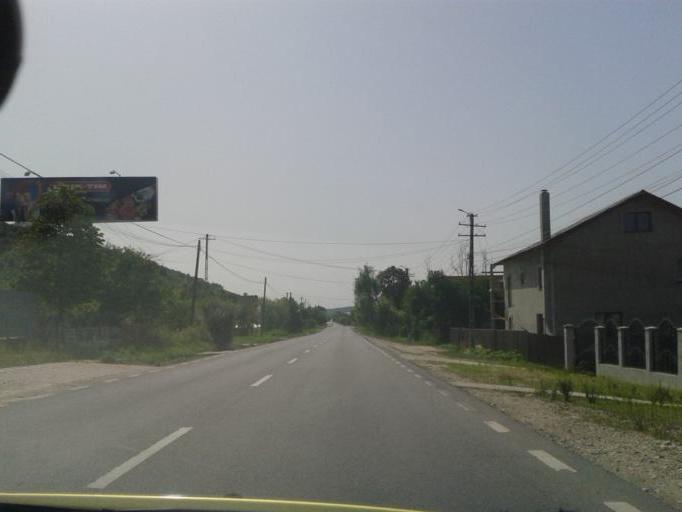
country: RO
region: Arges
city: Draganu-Olteni
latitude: 44.9090
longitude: 24.7256
